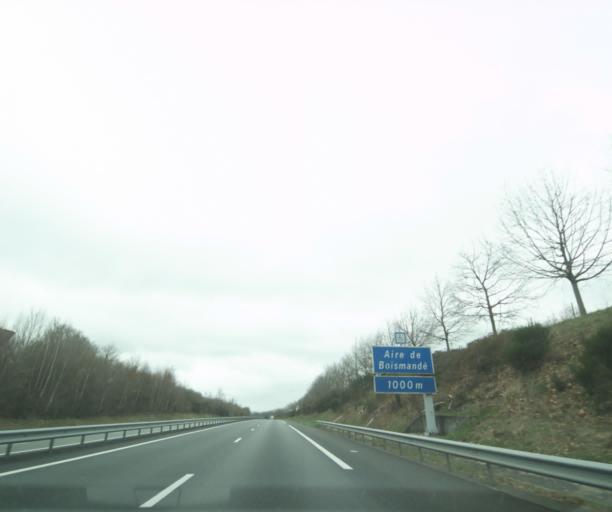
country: FR
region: Limousin
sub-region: Departement de la Haute-Vienne
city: Saint-Sulpice-les-Feuilles
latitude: 46.3267
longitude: 1.4180
